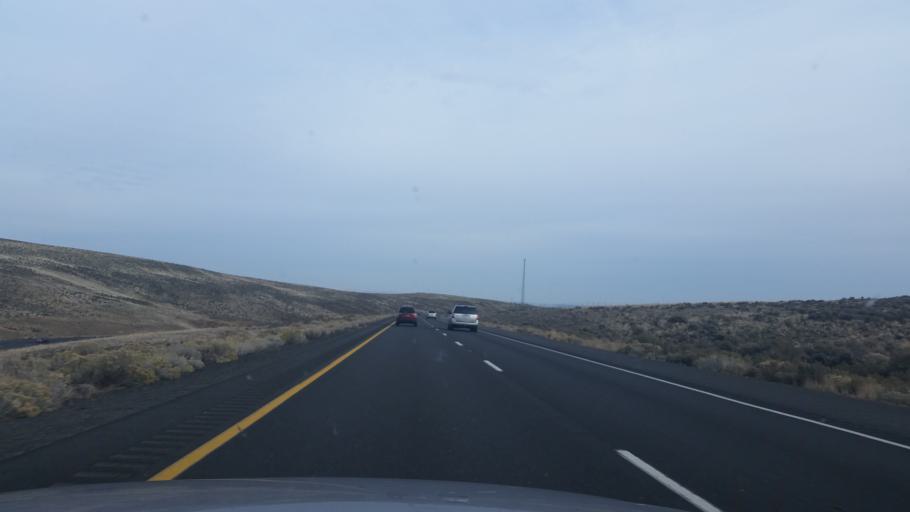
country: US
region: Washington
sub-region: Grant County
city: Mattawa
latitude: 46.9448
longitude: -120.0967
